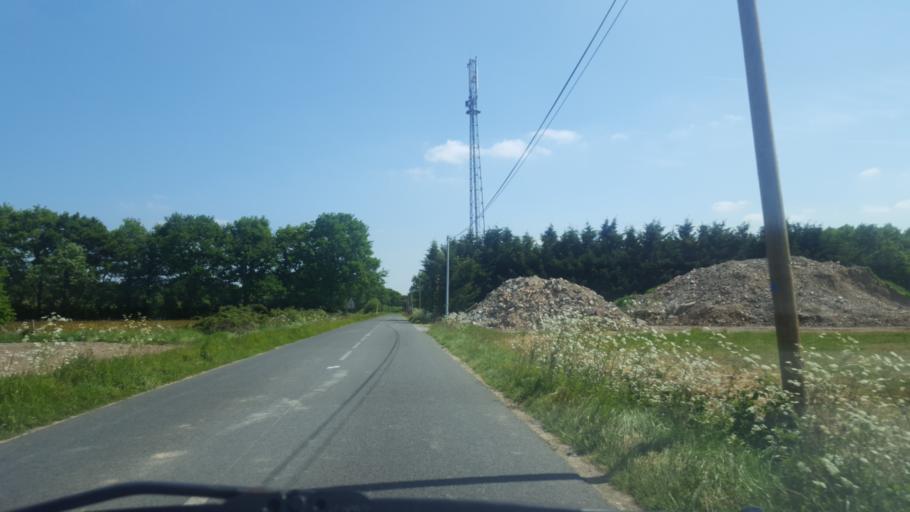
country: FR
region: Pays de la Loire
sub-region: Departement de la Loire-Atlantique
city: La Limouziniere
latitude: 47.0273
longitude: -1.5729
